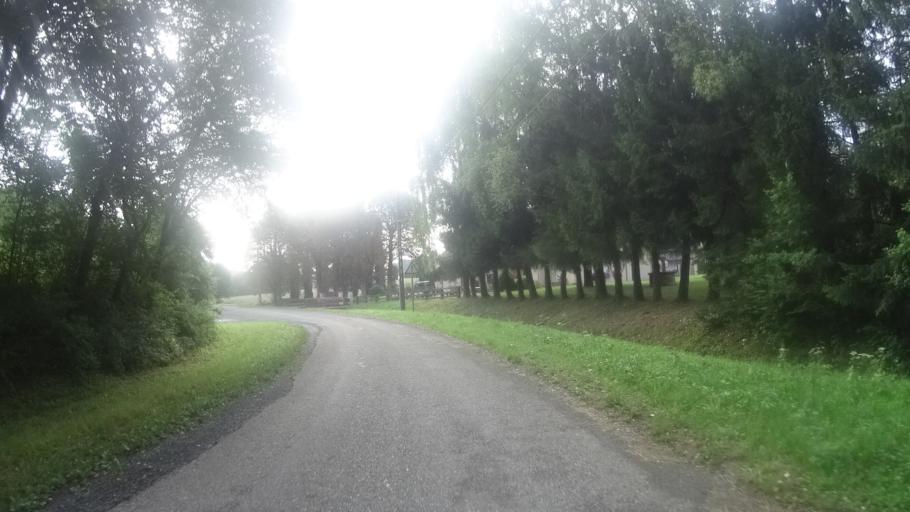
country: FR
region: Lorraine
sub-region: Departement de la Moselle
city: Niderviller
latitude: 48.7236
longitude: 7.1356
